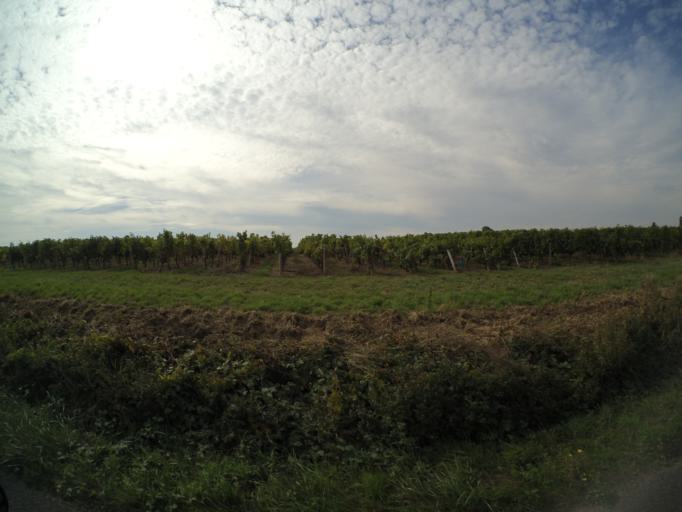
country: FR
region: Pays de la Loire
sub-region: Departement de Maine-et-Loire
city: Saint-Jean
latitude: 47.1964
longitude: -0.3641
